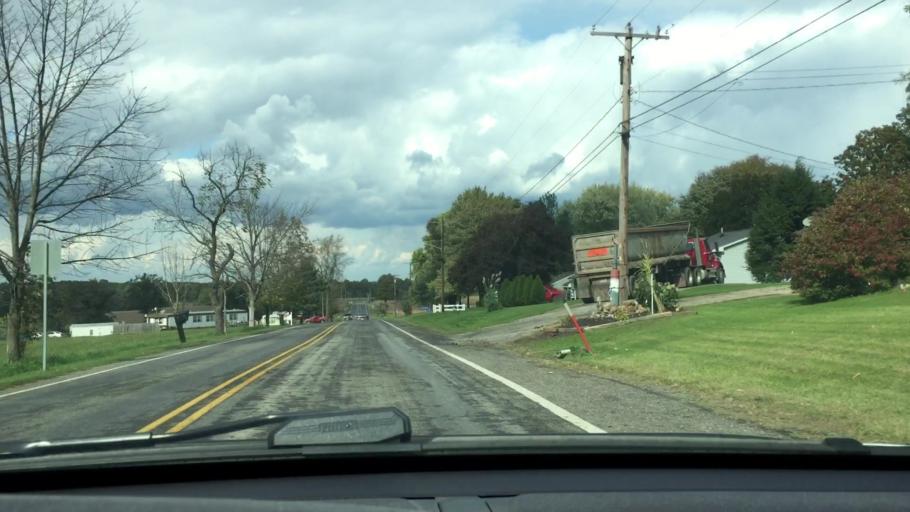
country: US
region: Pennsylvania
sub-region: Lawrence County
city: Bessemer
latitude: 40.9703
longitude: -80.4376
